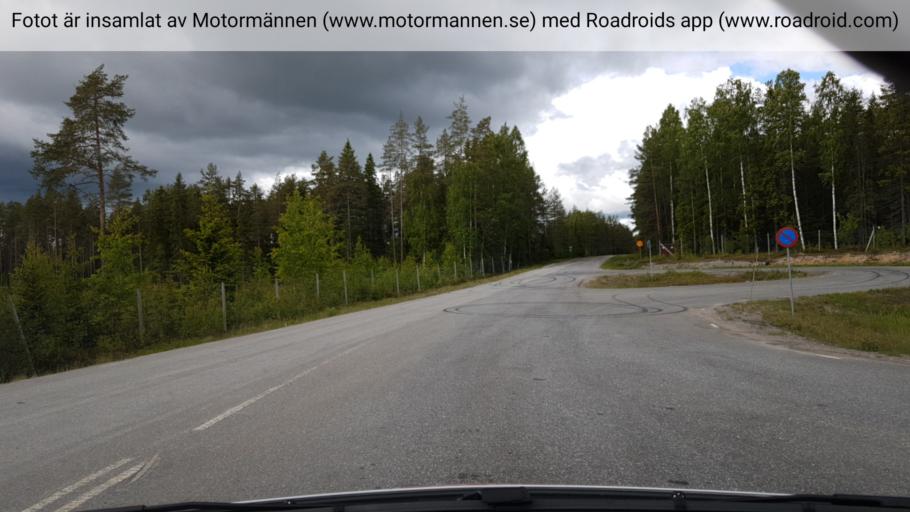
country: SE
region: Vaesterbotten
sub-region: Umea Kommun
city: Hoernefors
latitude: 63.7017
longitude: 20.0391
